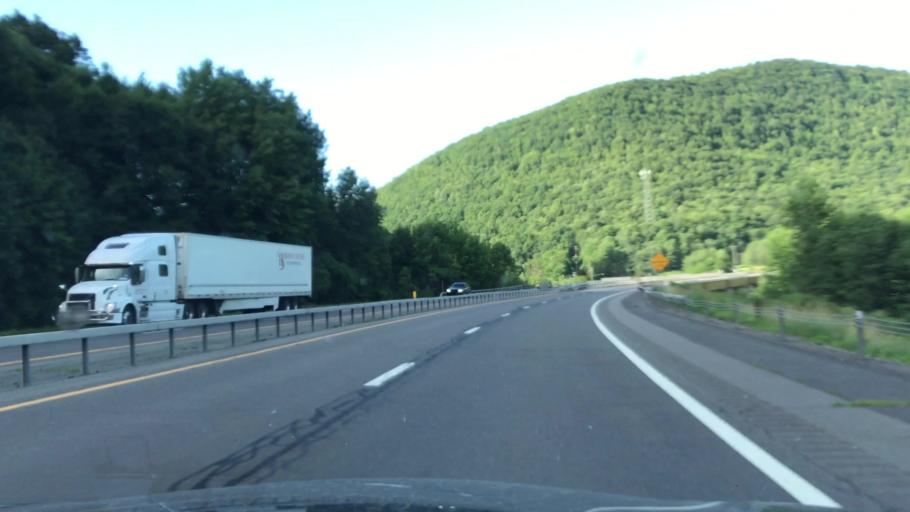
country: US
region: New York
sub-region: Delaware County
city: Hancock
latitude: 41.9627
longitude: -75.2650
